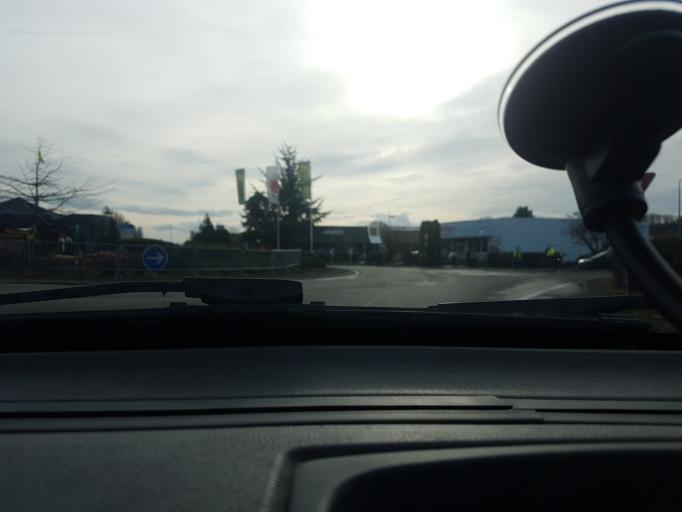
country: FR
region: Franche-Comte
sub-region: Territoire de Belfort
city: Andelnans
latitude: 47.6003
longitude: 6.8590
